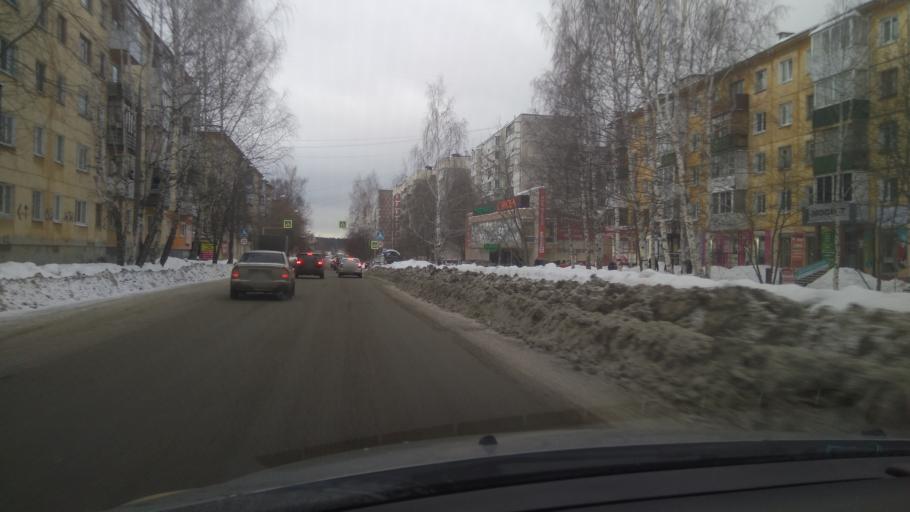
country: RU
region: Sverdlovsk
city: Verkhnyaya Pyshma
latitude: 56.9805
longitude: 60.5602
